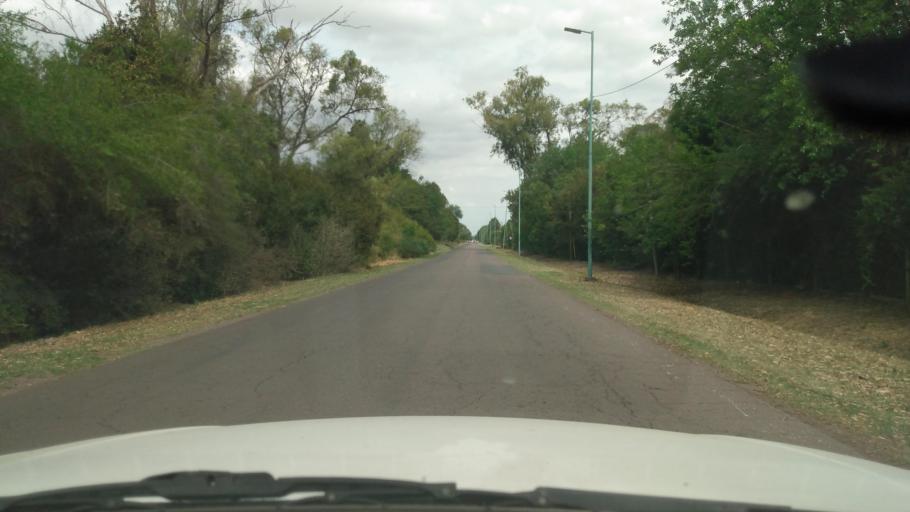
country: AR
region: Buenos Aires
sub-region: Partido de Lujan
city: Lujan
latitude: -34.5539
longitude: -59.1948
